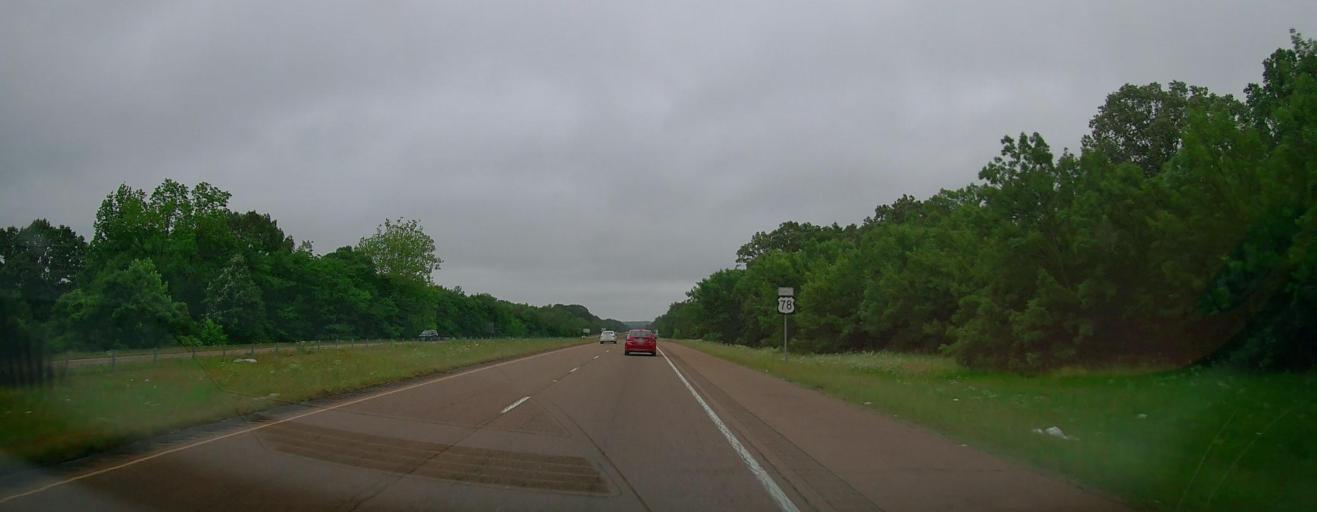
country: US
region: Mississippi
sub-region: De Soto County
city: Olive Branch
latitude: 34.9235
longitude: -89.7880
